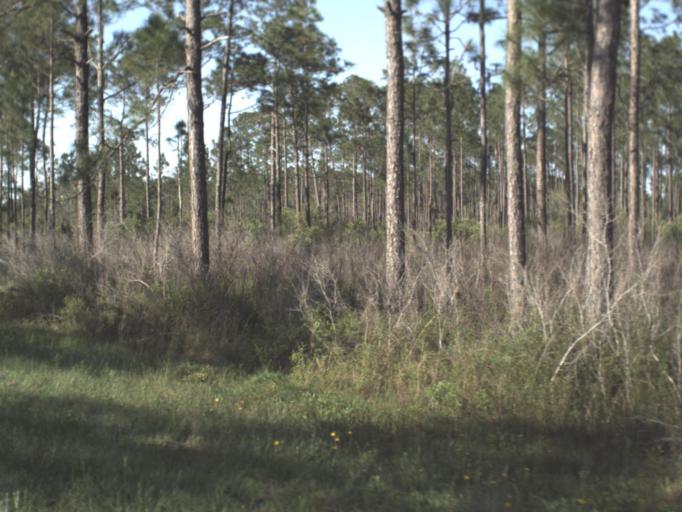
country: US
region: Florida
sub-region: Gulf County
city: Wewahitchka
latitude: 30.0882
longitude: -84.9839
